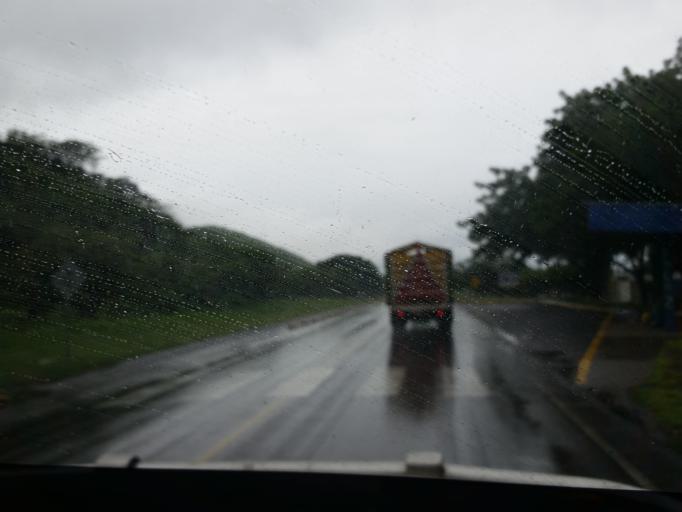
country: NI
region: Matagalpa
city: Ciudad Dario
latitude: 12.8783
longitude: -86.0843
